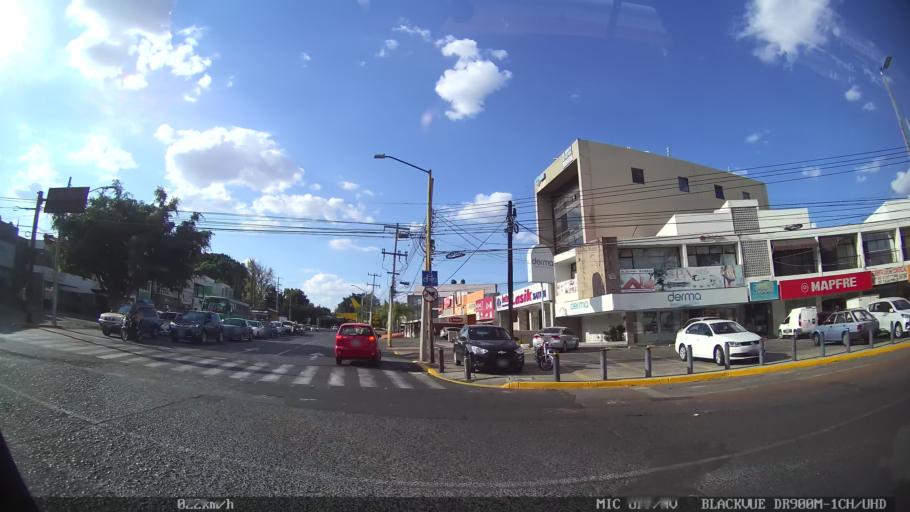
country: MX
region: Jalisco
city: Guadalajara
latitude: 20.6670
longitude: -103.3836
